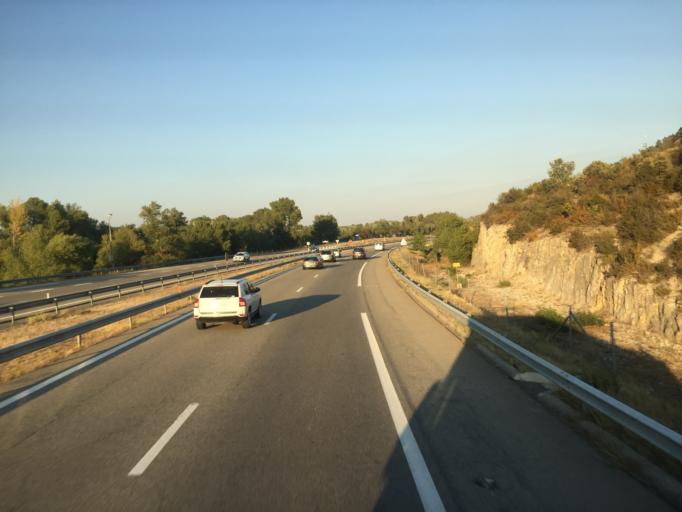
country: FR
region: Provence-Alpes-Cote d'Azur
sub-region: Departement du Vaucluse
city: Beaumont-de-Pertuis
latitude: 43.6909
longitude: 5.6776
